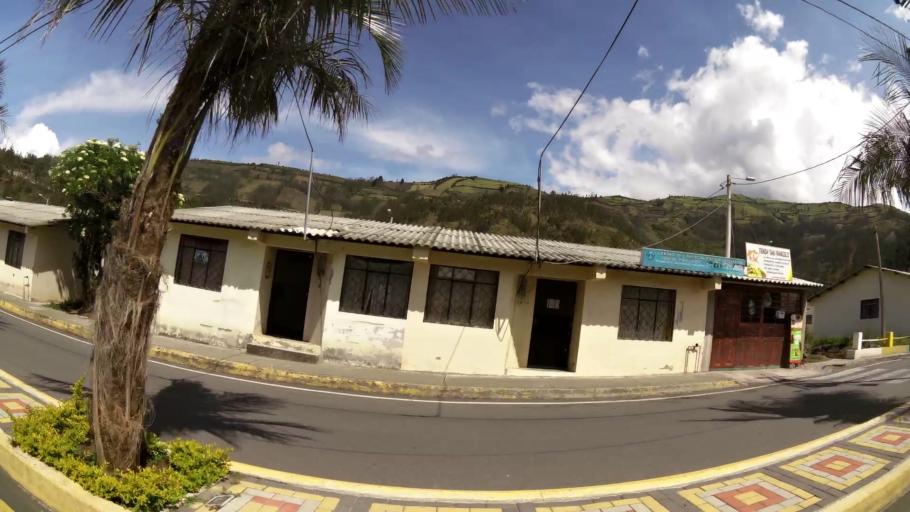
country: EC
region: Chimborazo
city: Guano
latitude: -1.5682
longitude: -78.5320
